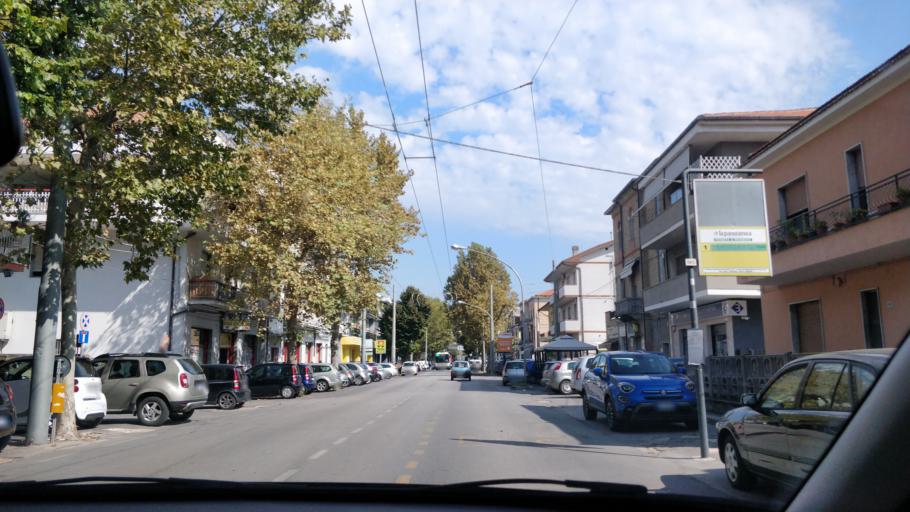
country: IT
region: Abruzzo
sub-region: Provincia di Chieti
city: Chieti
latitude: 42.3702
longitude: 14.1430
